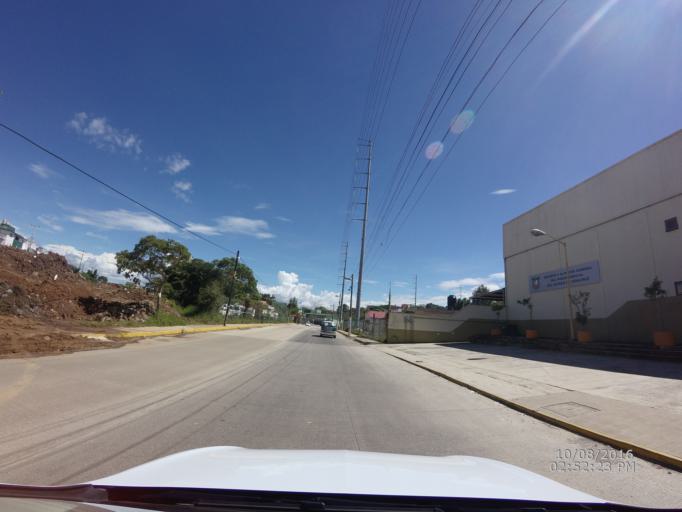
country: MX
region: Veracruz
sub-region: Xalapa
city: Colonia Santa Barbara
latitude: 19.5044
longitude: -96.8788
